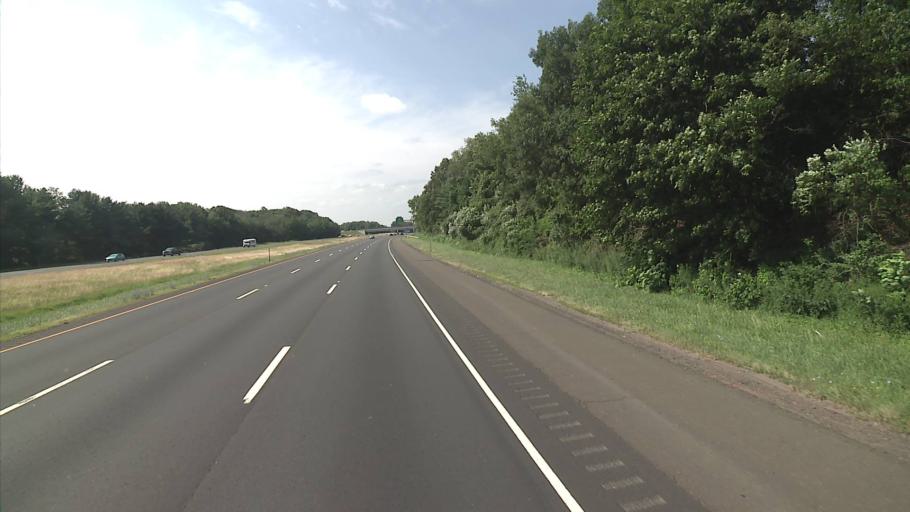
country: US
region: Connecticut
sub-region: New Haven County
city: Wallingford
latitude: 41.4864
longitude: -72.7681
